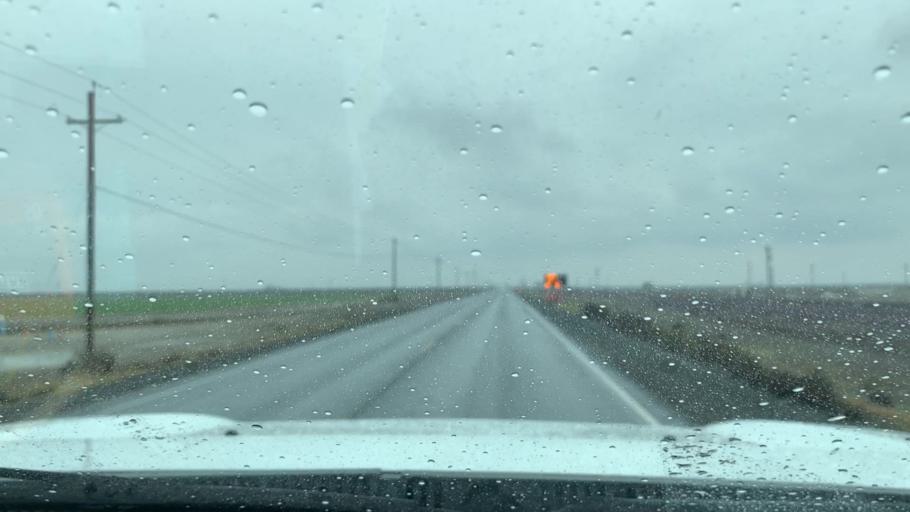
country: US
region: California
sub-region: Kings County
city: Corcoran
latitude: 36.0104
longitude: -119.4922
